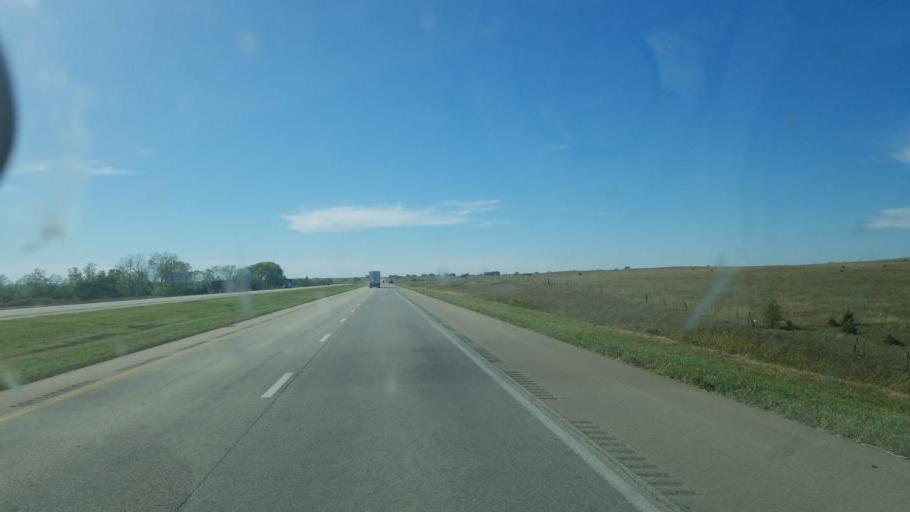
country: US
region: Kansas
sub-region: Saline County
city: Salina
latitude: 38.8783
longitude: -97.6910
